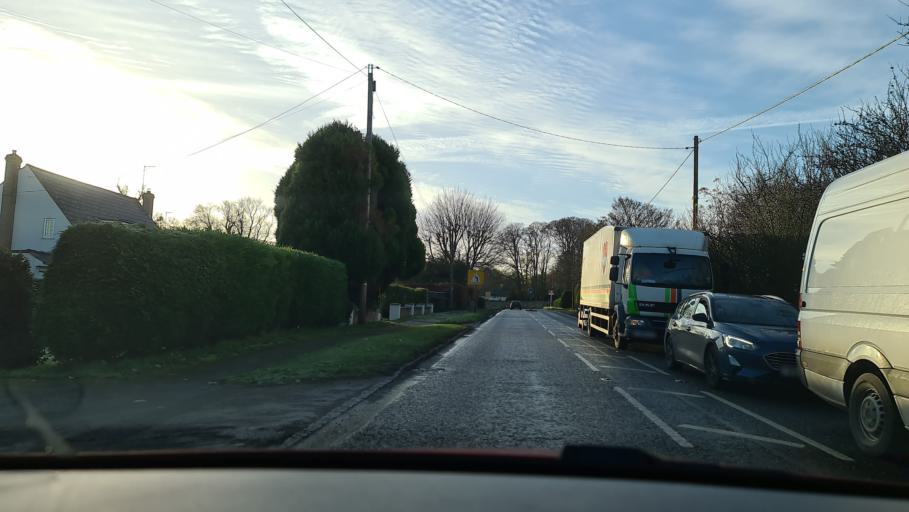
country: GB
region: England
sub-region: Buckinghamshire
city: Princes Risborough
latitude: 51.7535
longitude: -0.8083
